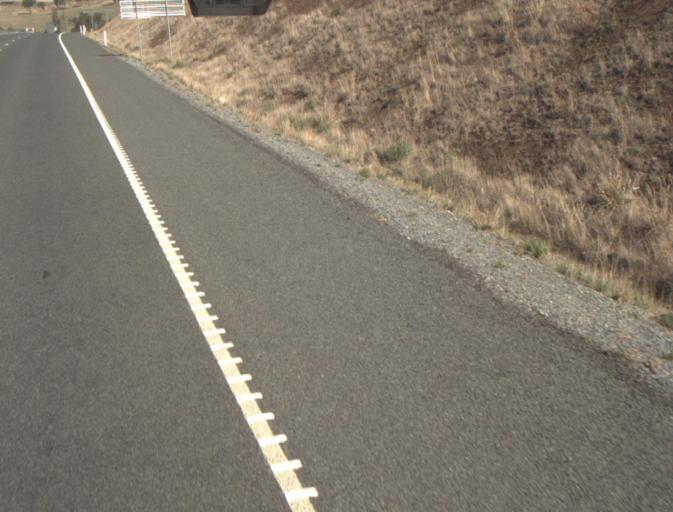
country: AU
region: Tasmania
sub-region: Launceston
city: Mayfield
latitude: -41.3553
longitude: 147.1044
